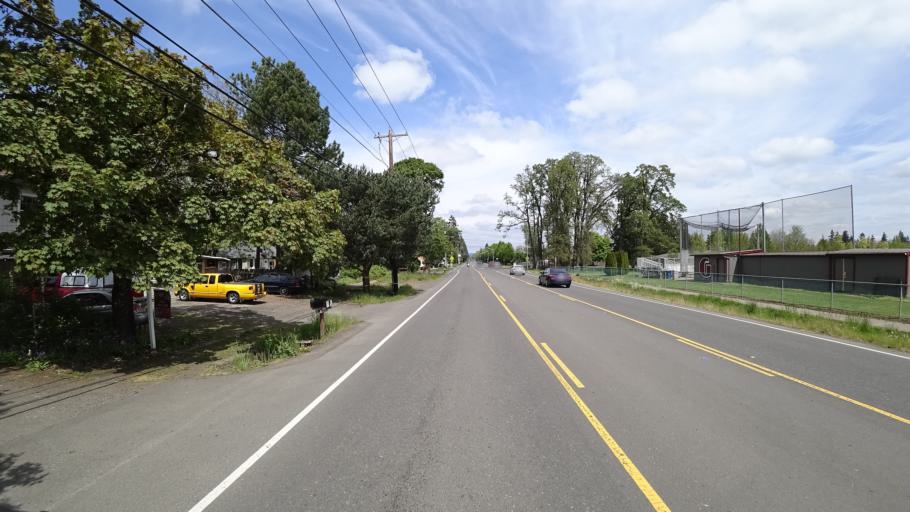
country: US
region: Oregon
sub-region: Washington County
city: Hillsboro
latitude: 45.5421
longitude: -122.9958
